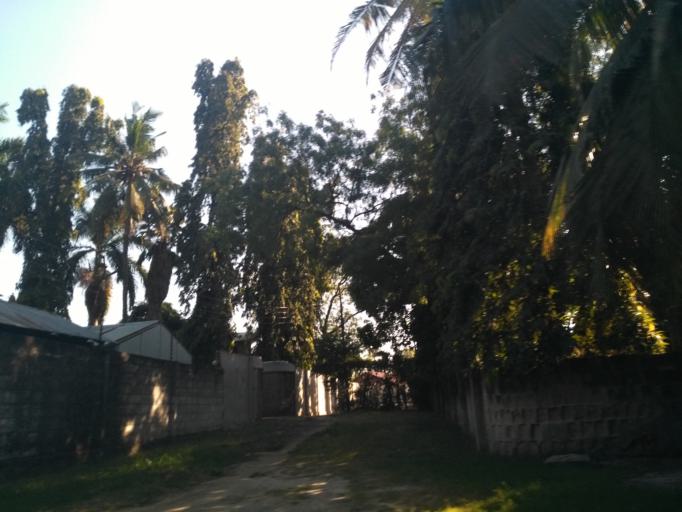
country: TZ
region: Dar es Salaam
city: Magomeni
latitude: -6.7655
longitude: 39.2554
